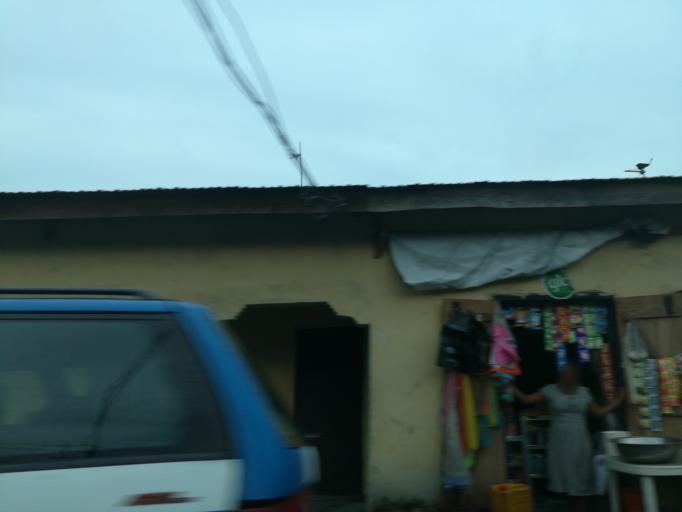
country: NG
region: Rivers
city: Port Harcourt
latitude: 4.7955
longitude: 6.9897
